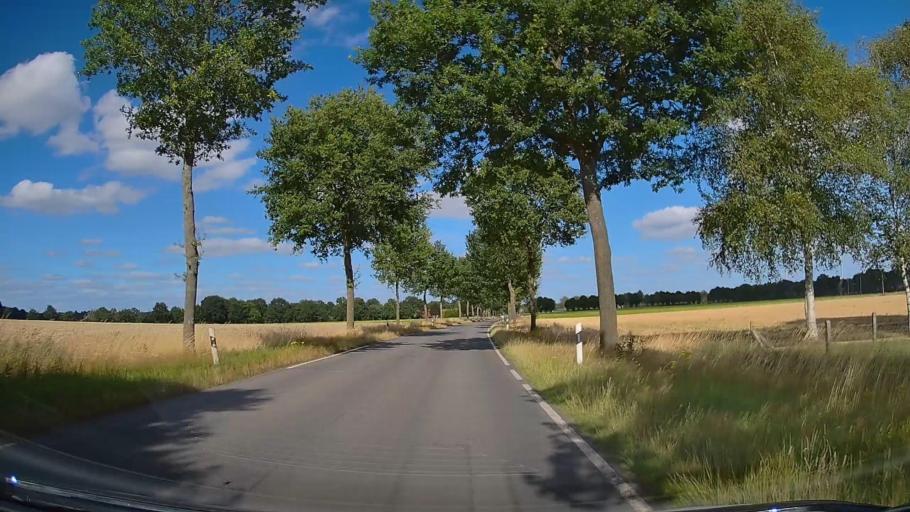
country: DE
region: Lower Saxony
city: Berge
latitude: 52.6232
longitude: 7.7623
